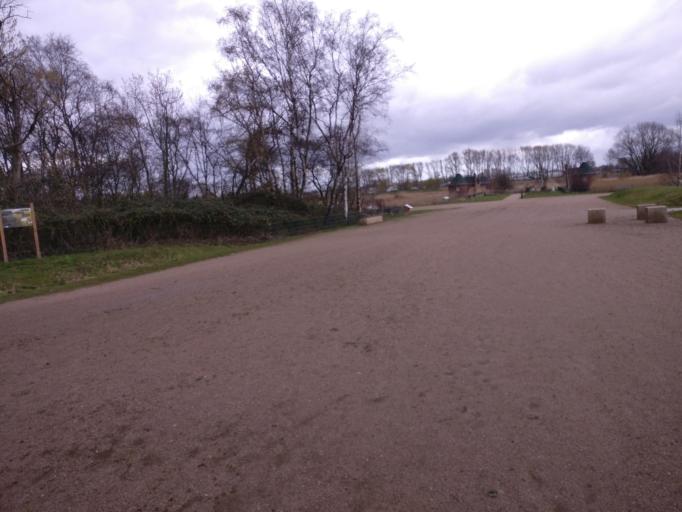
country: DE
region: Hamburg
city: Rothenburgsort
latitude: 53.5247
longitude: 10.0534
